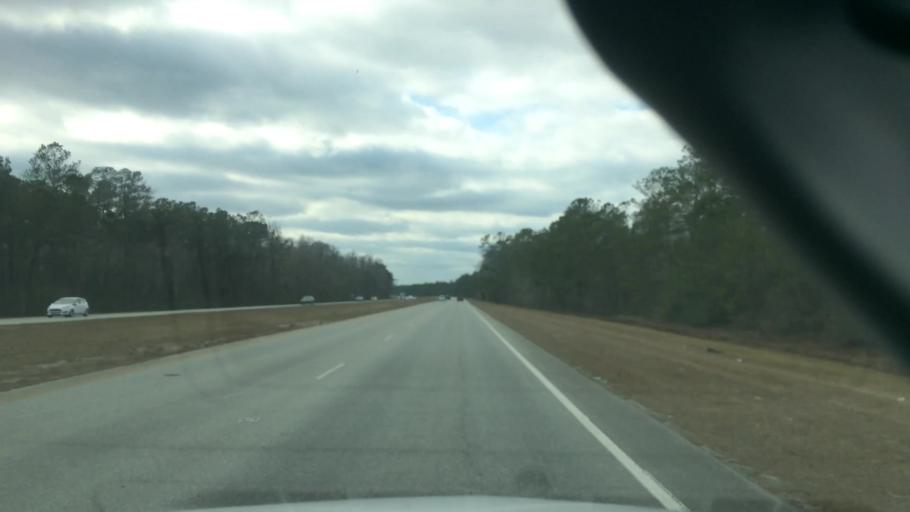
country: US
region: North Carolina
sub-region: Brunswick County
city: Bolivia
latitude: 34.0768
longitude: -78.1508
